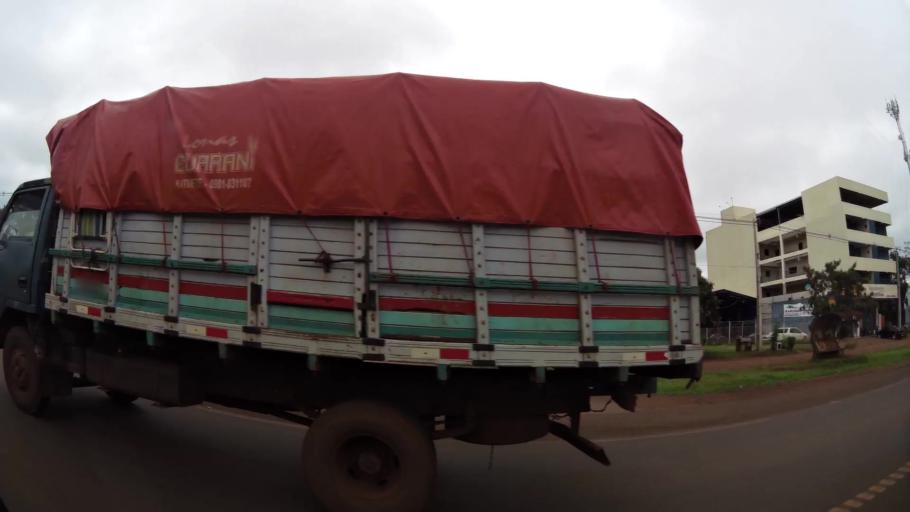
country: PY
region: Alto Parana
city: Ciudad del Este
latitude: -25.4922
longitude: -54.7363
